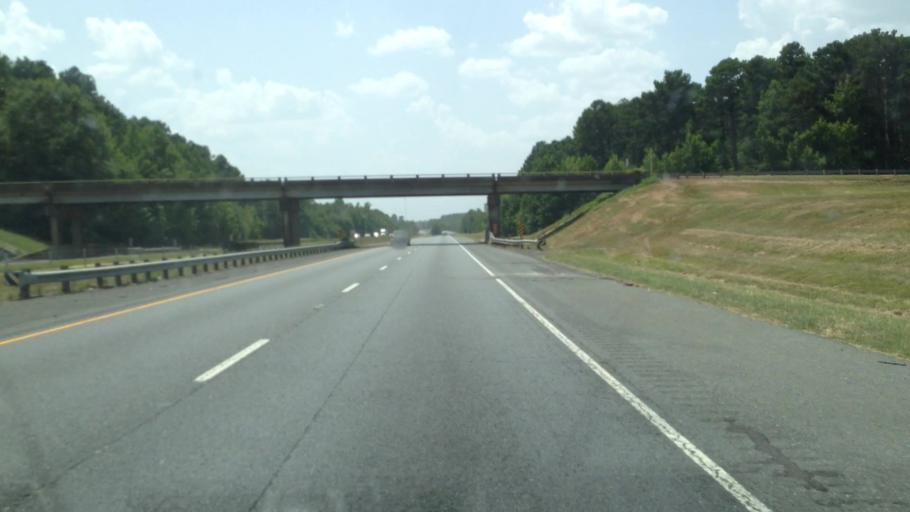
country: US
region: Louisiana
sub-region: Lincoln Parish
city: Grambling
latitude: 32.5468
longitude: -92.7655
